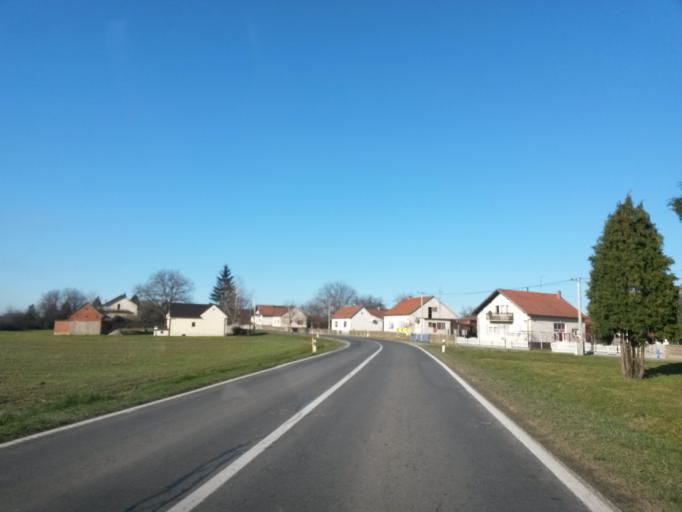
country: HR
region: Virovitick-Podravska
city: Suhopolje
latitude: 45.7747
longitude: 17.5662
